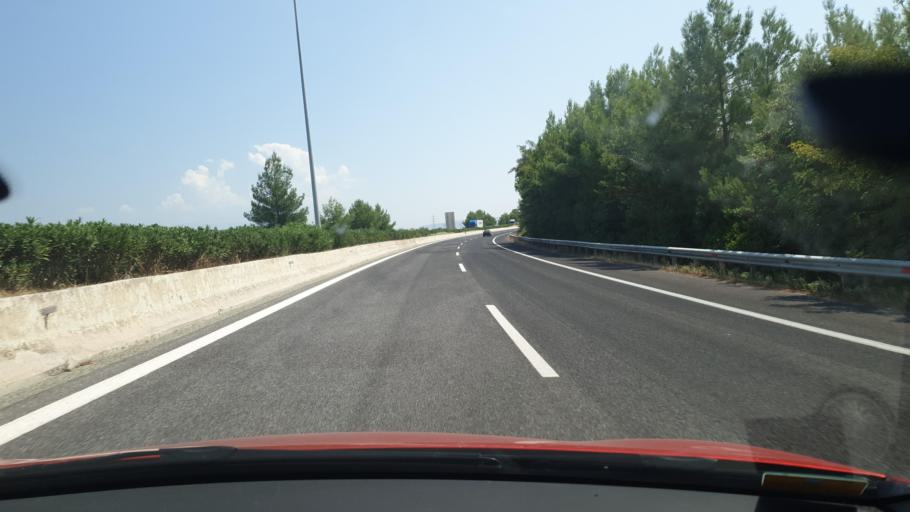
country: GR
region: Thessaly
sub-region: Nomos Magnisias
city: Stefanoviki
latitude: 39.4925
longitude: 22.6308
